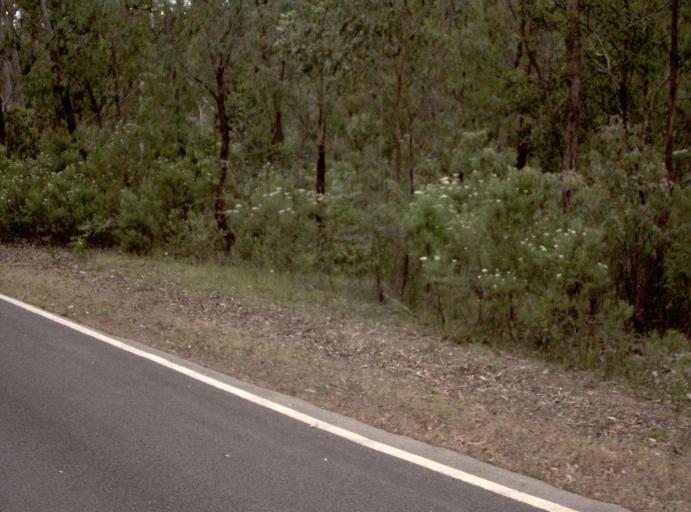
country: AU
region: Victoria
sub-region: East Gippsland
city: Bairnsdale
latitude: -37.6406
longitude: 147.2639
